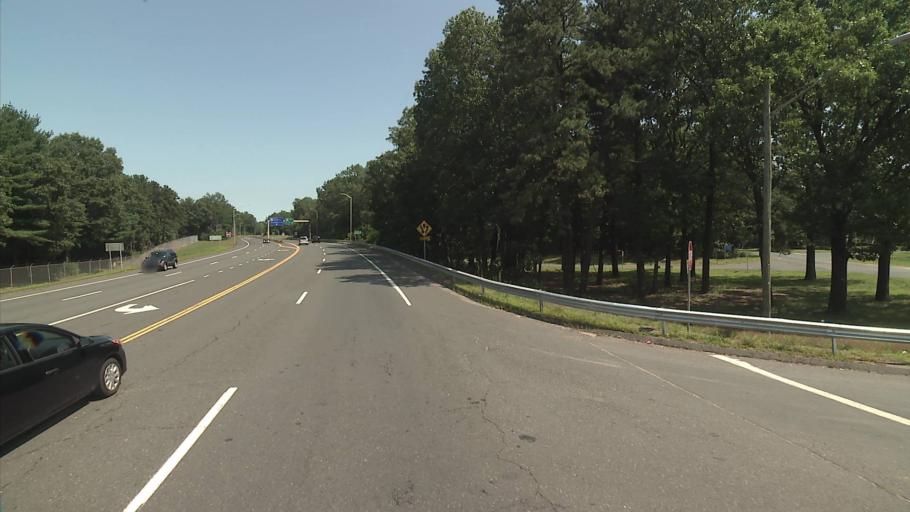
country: US
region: Connecticut
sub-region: Hartford County
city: Tariffville
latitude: 41.9252
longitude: -72.7034
